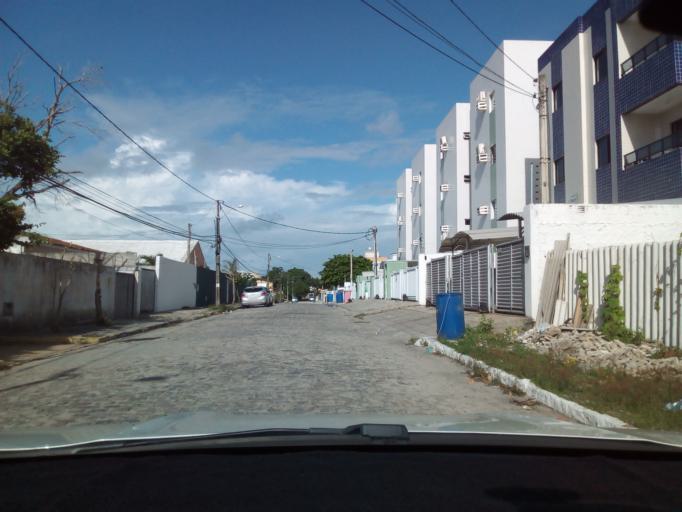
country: BR
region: Paraiba
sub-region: Joao Pessoa
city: Joao Pessoa
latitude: -7.1537
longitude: -34.8277
